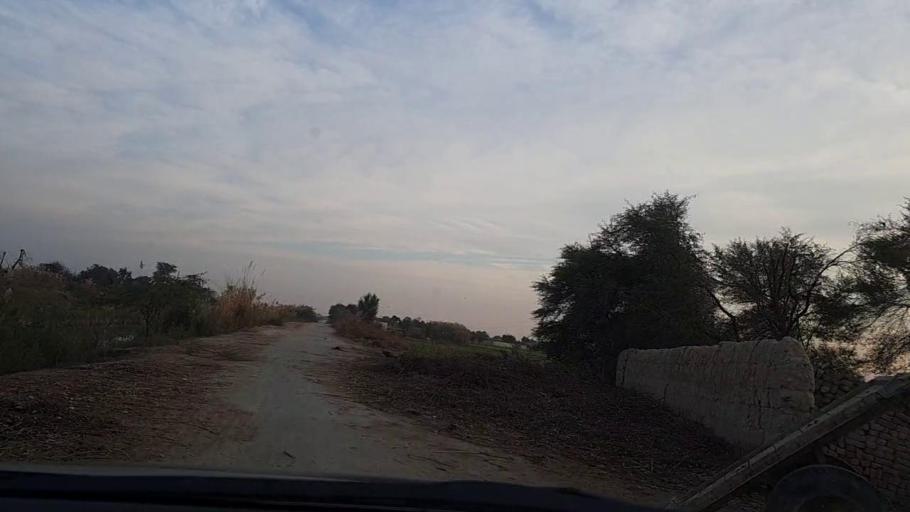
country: PK
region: Sindh
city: Sakrand
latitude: 26.1809
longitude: 68.3412
